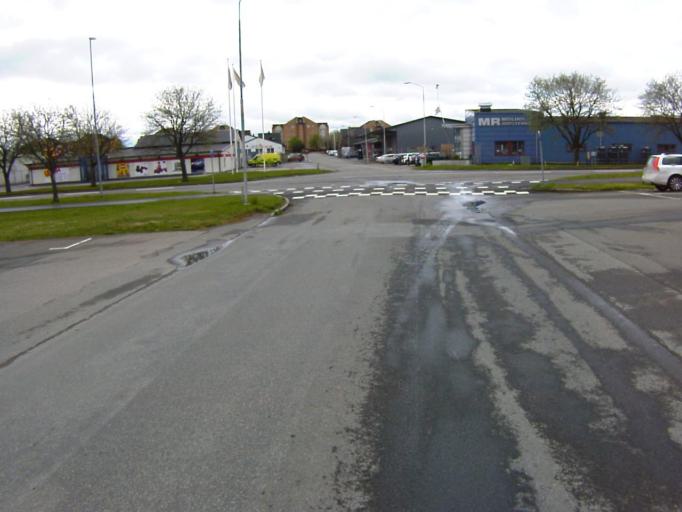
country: SE
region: Skane
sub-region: Kristianstads Kommun
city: Kristianstad
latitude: 56.0233
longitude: 14.1386
